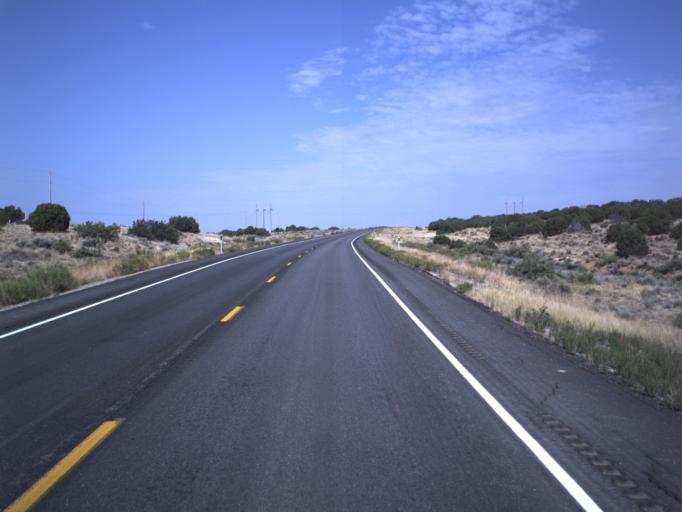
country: US
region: Utah
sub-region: Uintah County
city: Naples
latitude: 40.3202
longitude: -109.2528
